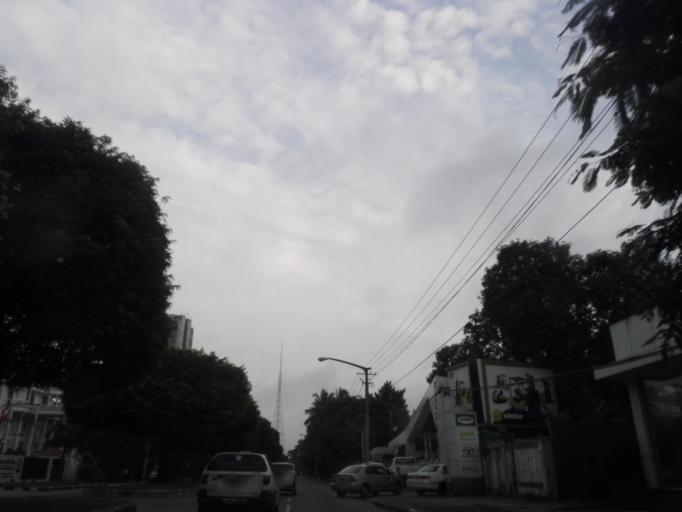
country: MM
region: Yangon
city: Yangon
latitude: 16.8092
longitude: 96.1386
